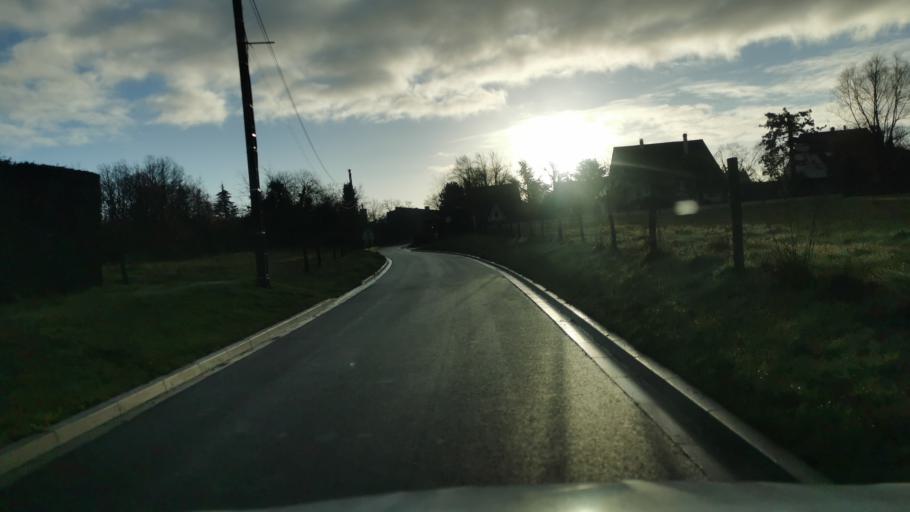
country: FR
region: Ile-de-France
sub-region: Departement des Yvelines
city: Bazainville
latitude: 48.8271
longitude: 1.6312
